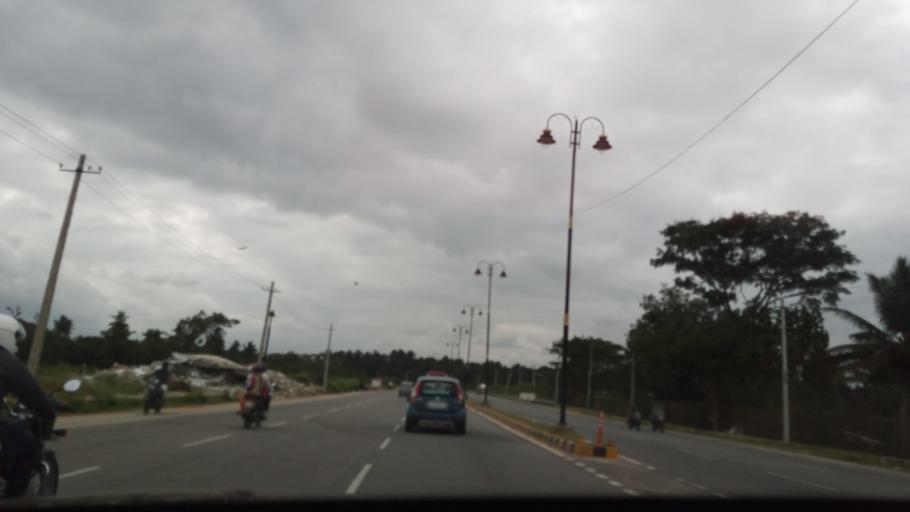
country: IN
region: Karnataka
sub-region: Mysore
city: Mysore
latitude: 12.3443
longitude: 76.6589
